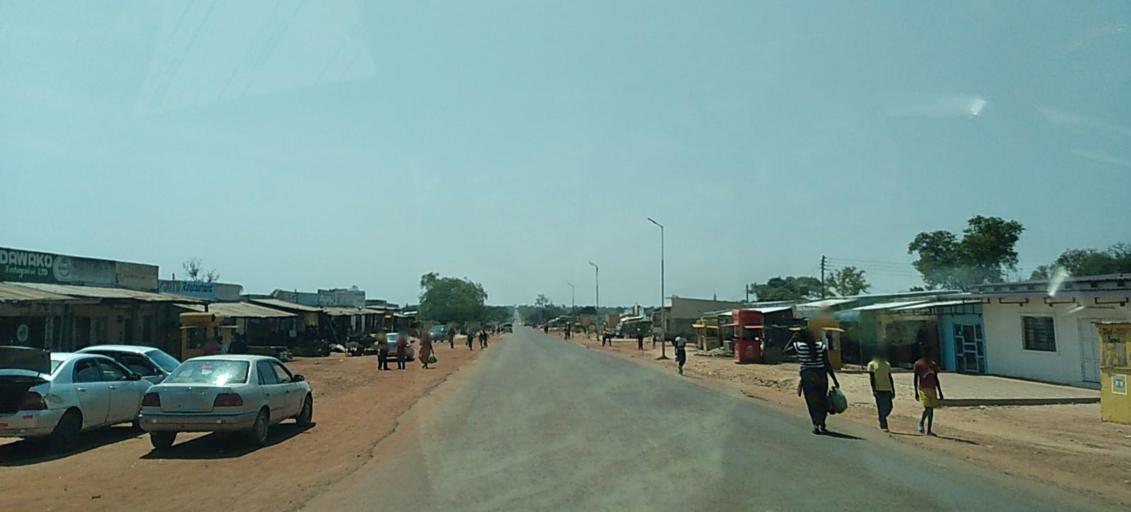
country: ZM
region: North-Western
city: Solwezi
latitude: -12.3137
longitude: 25.8512
